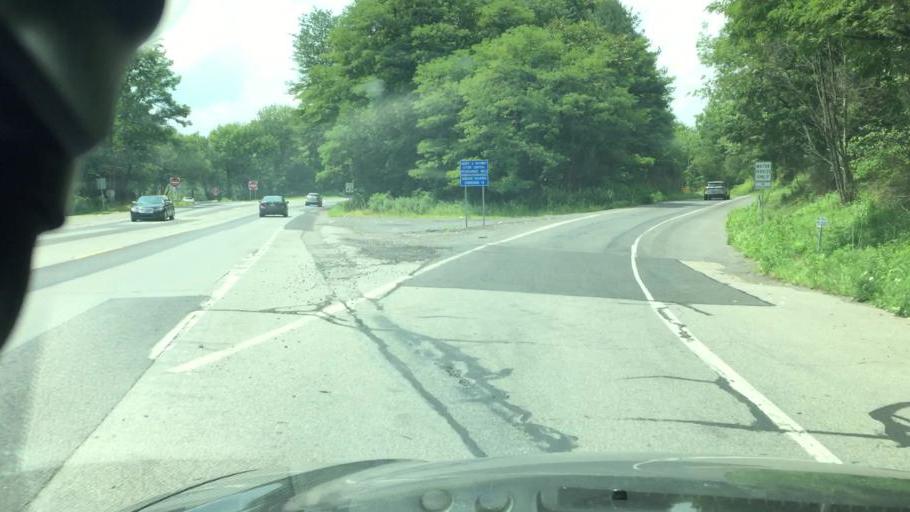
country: US
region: Pennsylvania
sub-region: Monroe County
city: Arlington Heights
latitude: 40.9869
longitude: -75.2287
